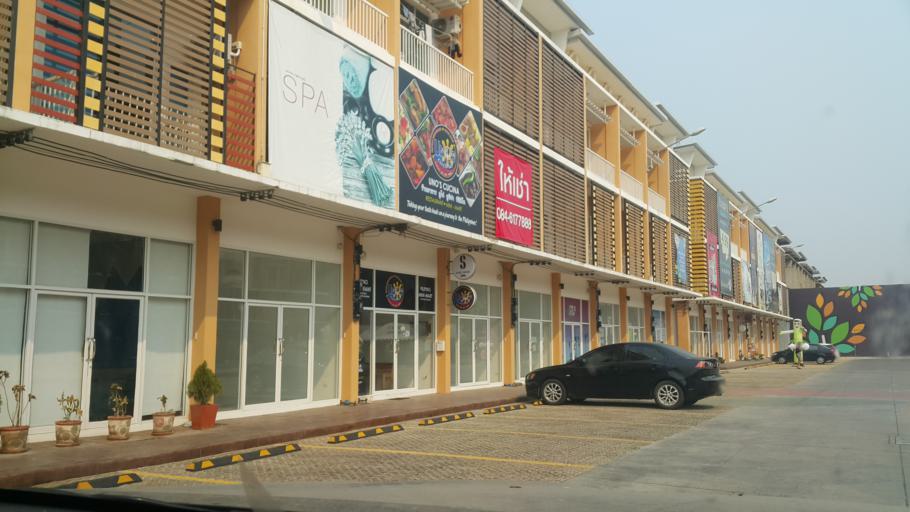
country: TH
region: Chiang Mai
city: Hang Dong
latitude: 18.7248
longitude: 98.9483
